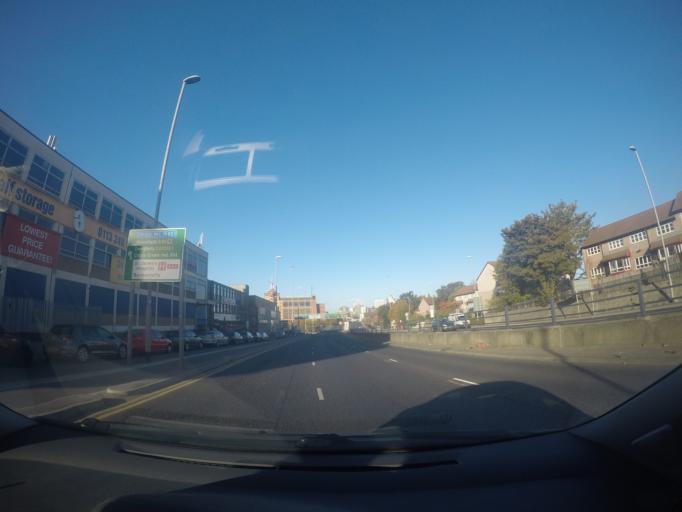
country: GB
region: England
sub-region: City and Borough of Leeds
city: Leeds
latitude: 53.7980
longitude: -1.5243
